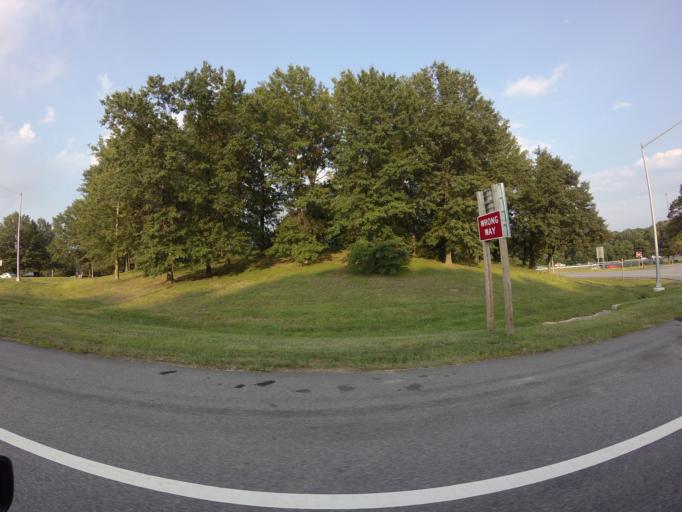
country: US
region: Maryland
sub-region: Howard County
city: Savage
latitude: 39.1445
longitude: -76.8465
